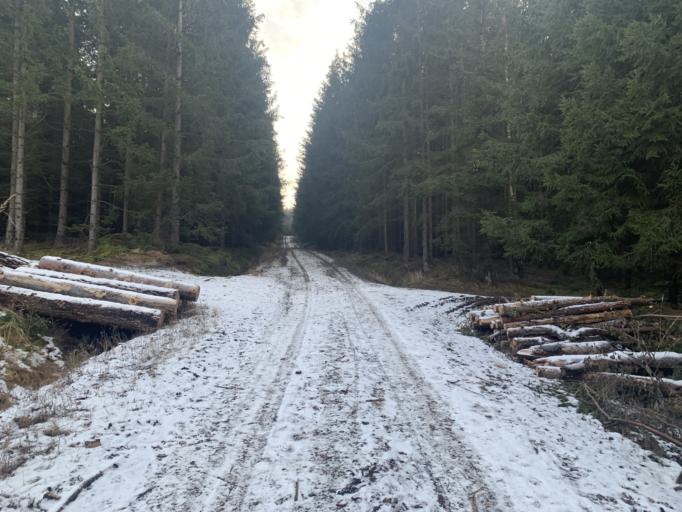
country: CZ
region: Plzensky
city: Zbiroh
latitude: 49.8242
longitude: 13.7972
